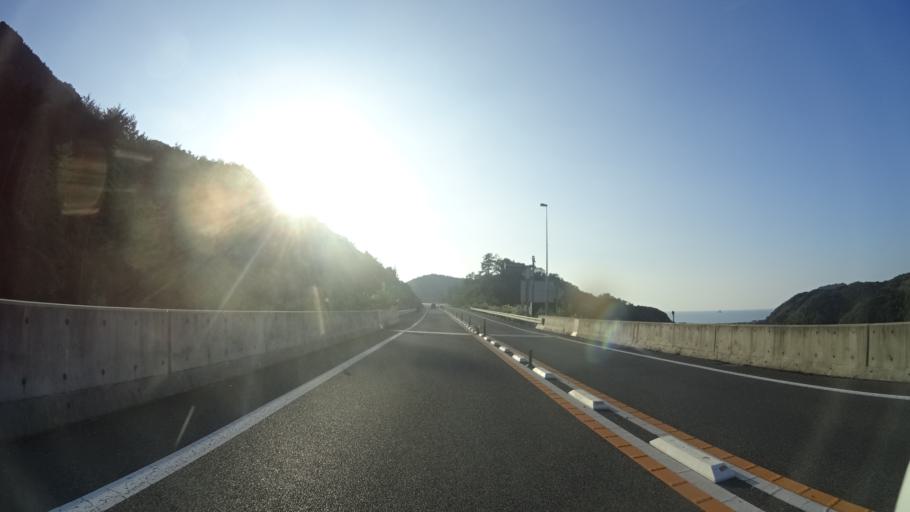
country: JP
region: Yamaguchi
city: Hagi
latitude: 34.3879
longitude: 131.3376
